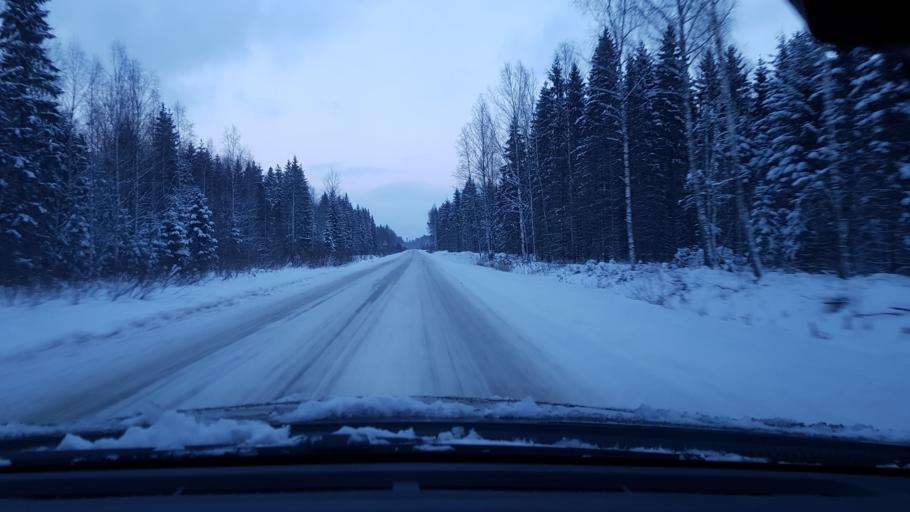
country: EE
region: Raplamaa
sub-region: Jaervakandi vald
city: Jarvakandi
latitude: 58.7987
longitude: 24.8723
